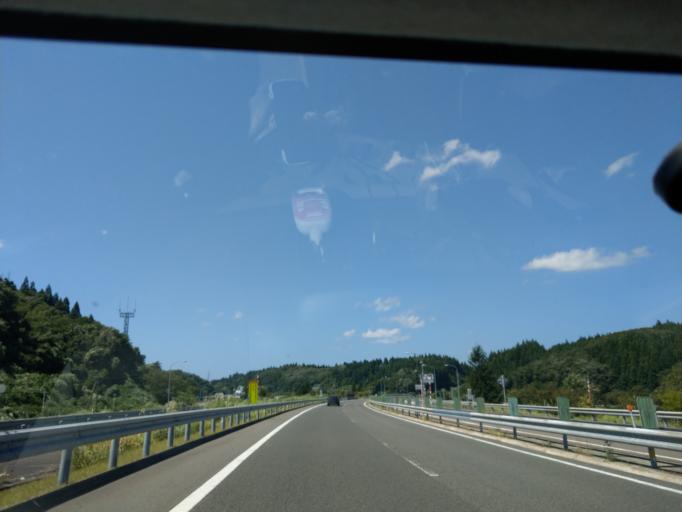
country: JP
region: Akita
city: Akita
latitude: 39.6583
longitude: 140.1931
